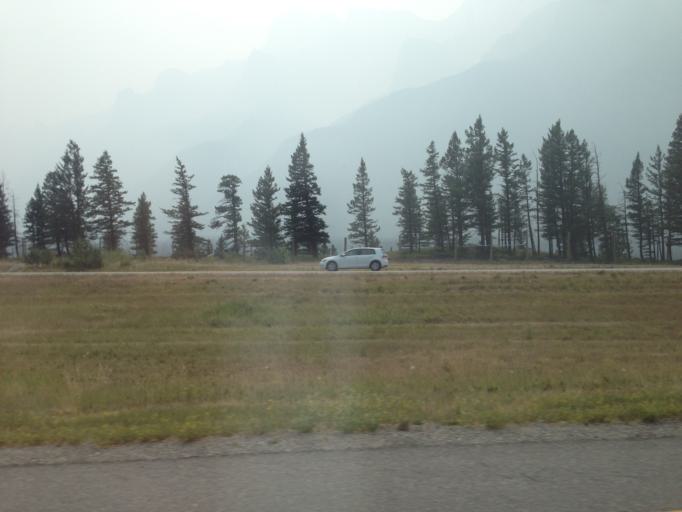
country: CA
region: Alberta
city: Banff
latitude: 51.1677
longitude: -115.4550
